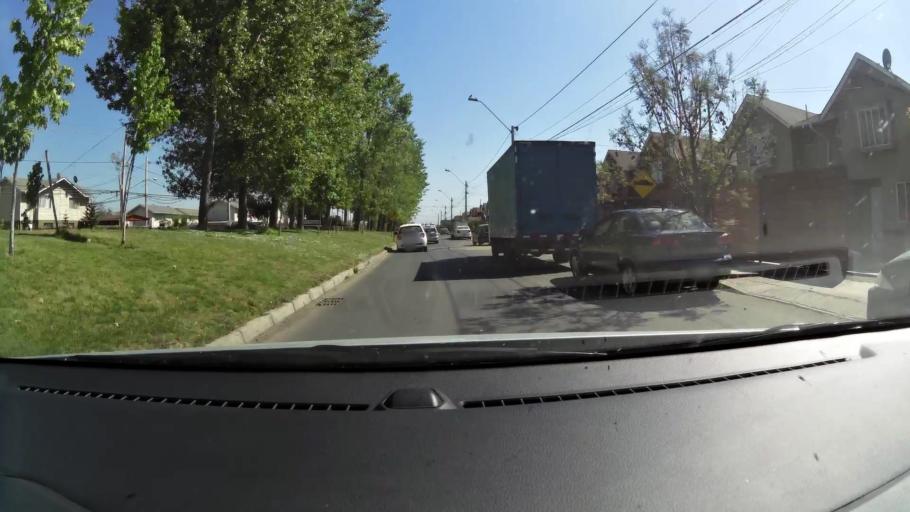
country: CL
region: Santiago Metropolitan
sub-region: Provincia de Maipo
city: San Bernardo
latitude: -33.6119
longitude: -70.6876
